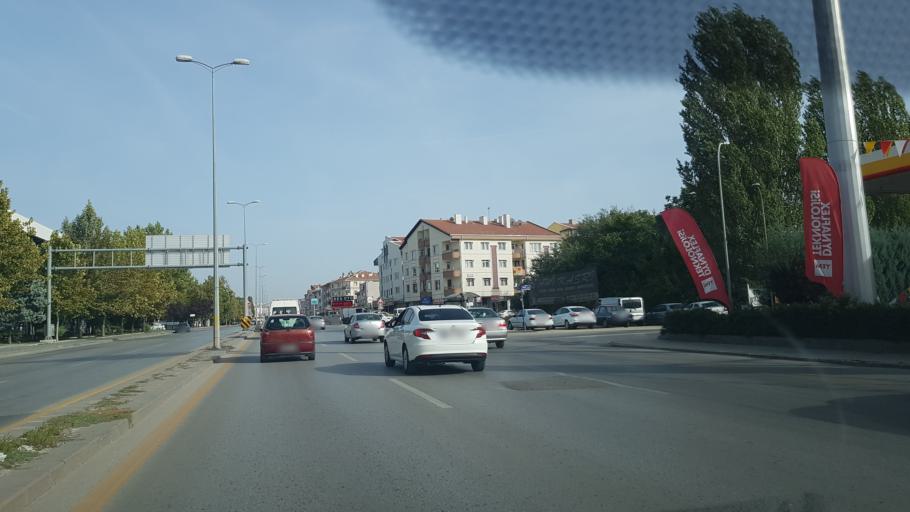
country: TR
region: Ankara
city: Etimesgut
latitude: 39.9555
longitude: 32.6285
